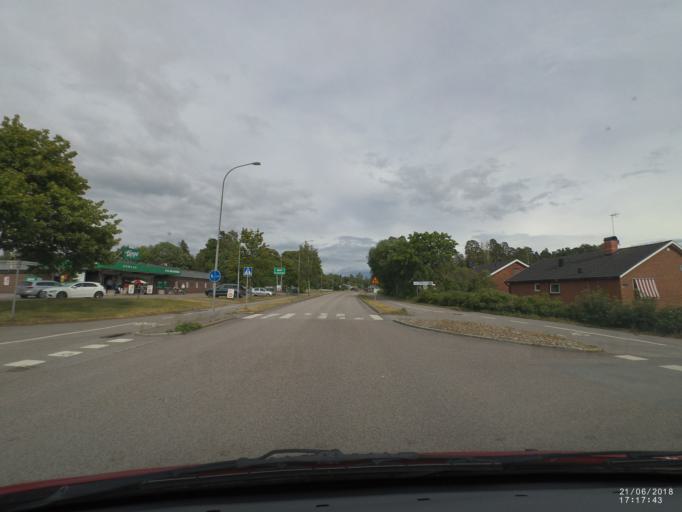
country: SE
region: Soedermanland
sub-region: Nykopings Kommun
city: Nykoping
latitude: 58.7537
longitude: 17.0515
